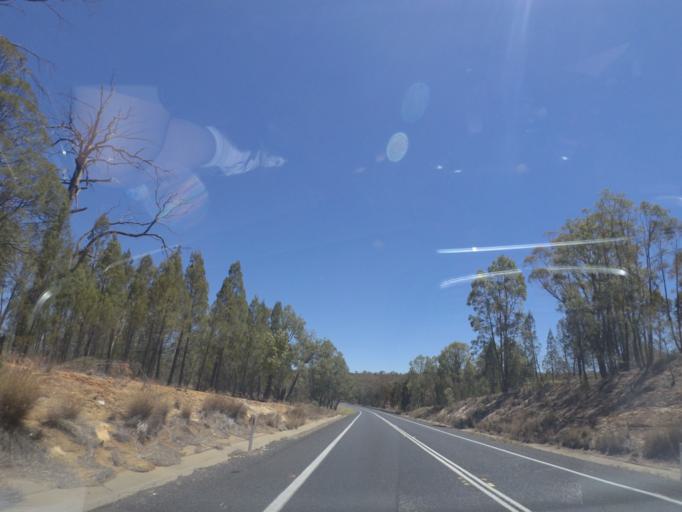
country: AU
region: New South Wales
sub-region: Warrumbungle Shire
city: Coonabarabran
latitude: -31.3290
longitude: 149.3048
